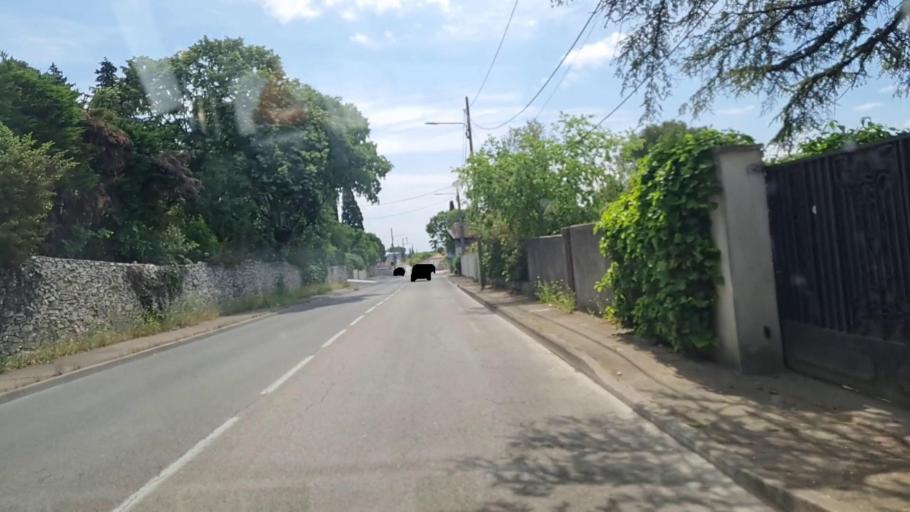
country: FR
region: Languedoc-Roussillon
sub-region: Departement du Gard
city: Nimes
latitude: 43.8389
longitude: 4.3230
